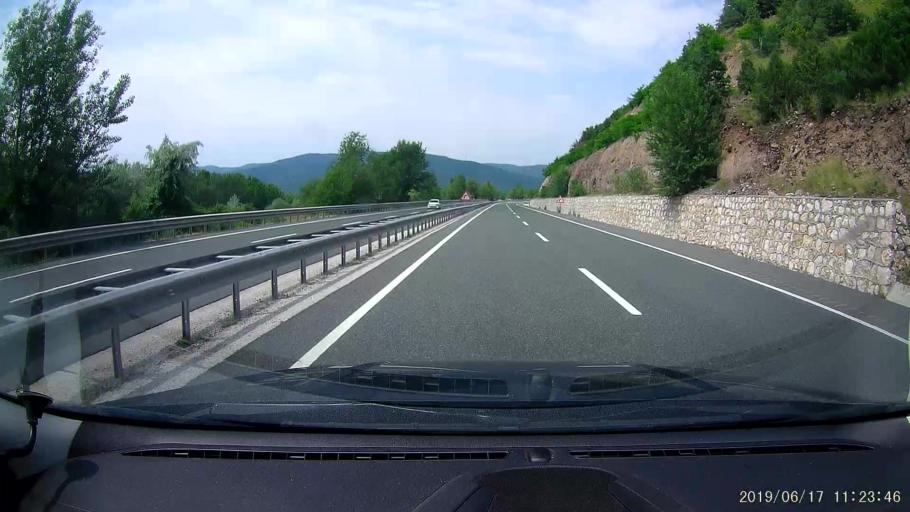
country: TR
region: Cankiri
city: Ilgaz
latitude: 40.8845
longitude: 33.7233
